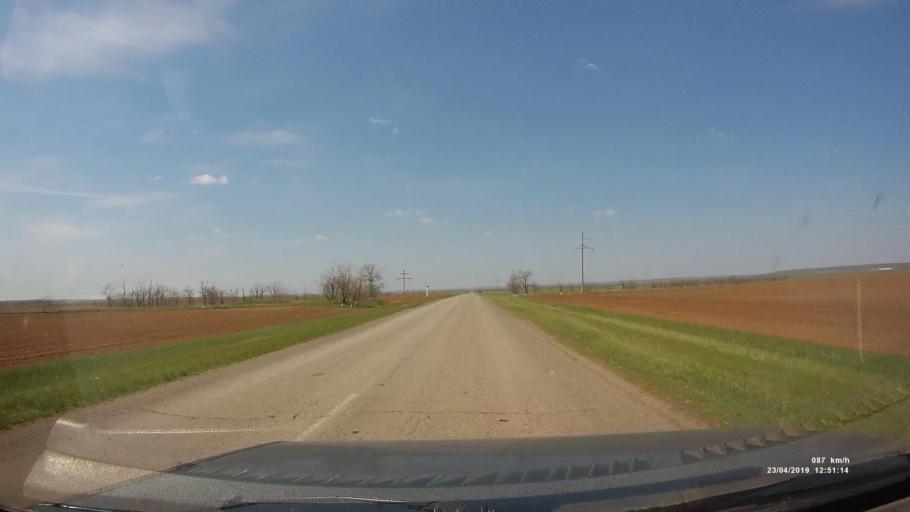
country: RU
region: Kalmykiya
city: Yashalta
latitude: 46.5531
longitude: 42.6253
